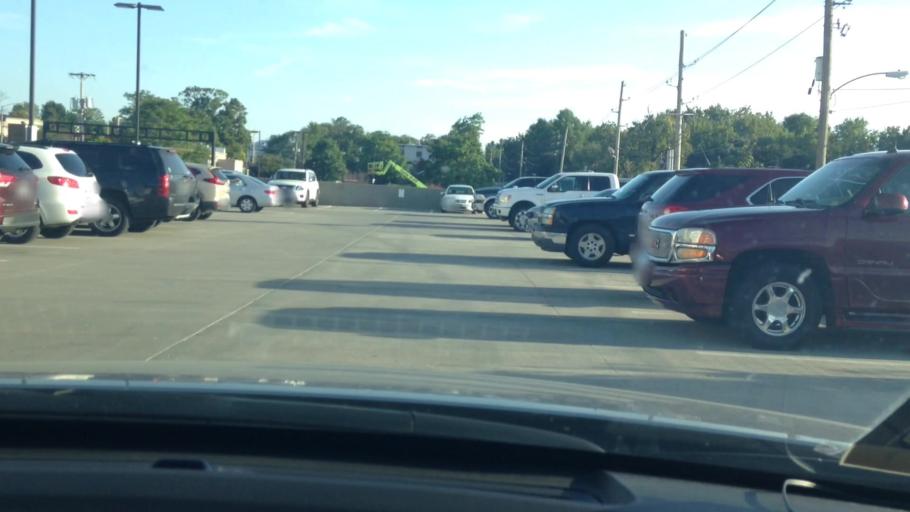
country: US
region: Kansas
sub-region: Johnson County
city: Westwood
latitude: 39.0560
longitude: -94.6129
